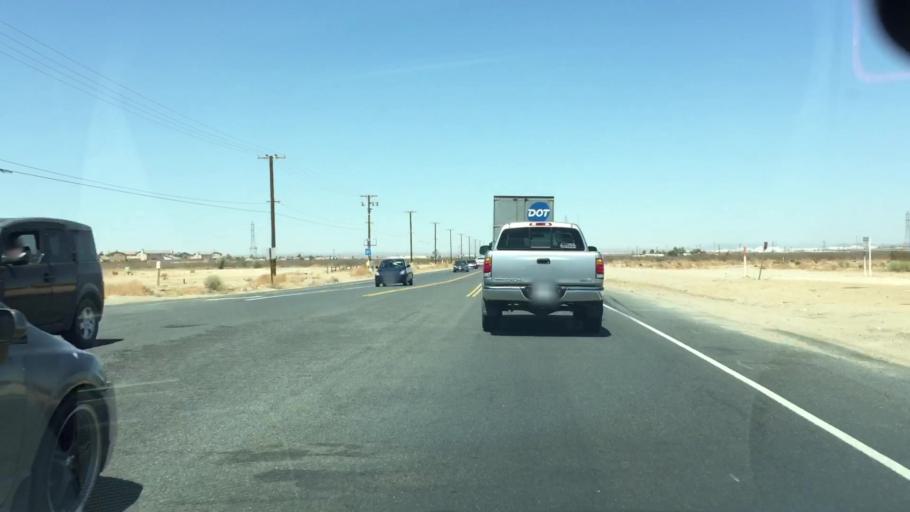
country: US
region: California
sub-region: San Bernardino County
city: Mountain View Acres
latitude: 34.5140
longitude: -117.3994
